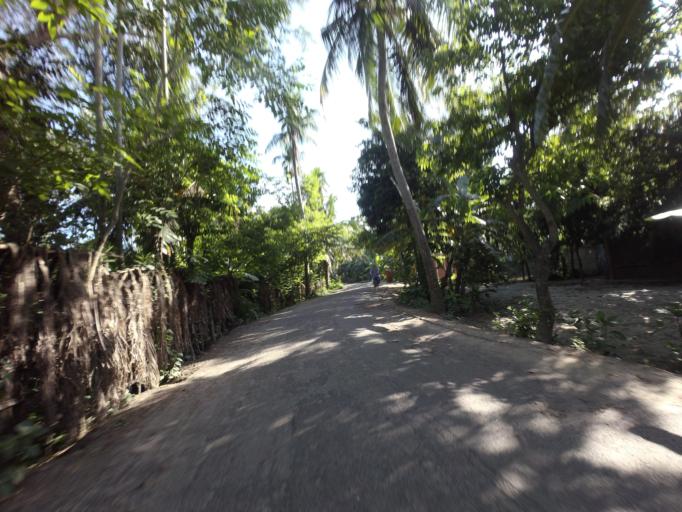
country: BD
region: Khulna
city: Kalia
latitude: 23.0028
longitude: 89.5789
